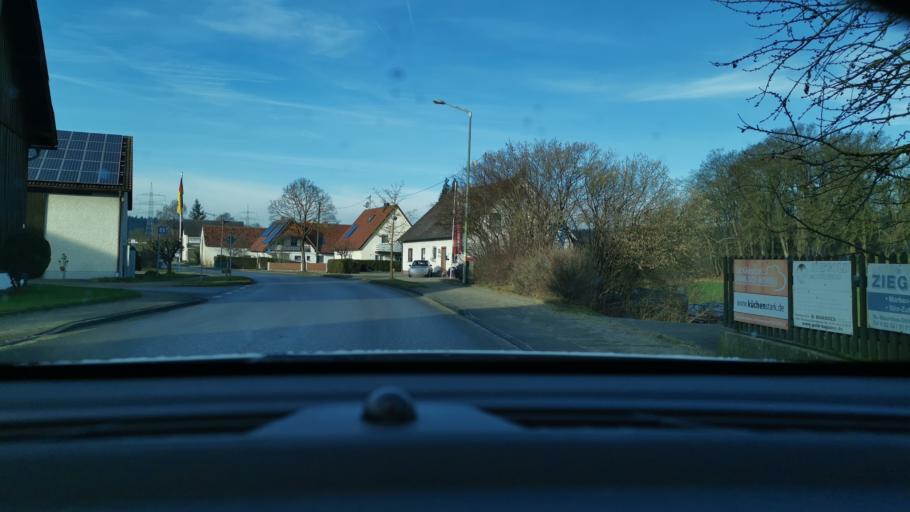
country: DE
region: Bavaria
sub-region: Swabia
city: Hollenbach
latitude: 48.5039
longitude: 11.0595
